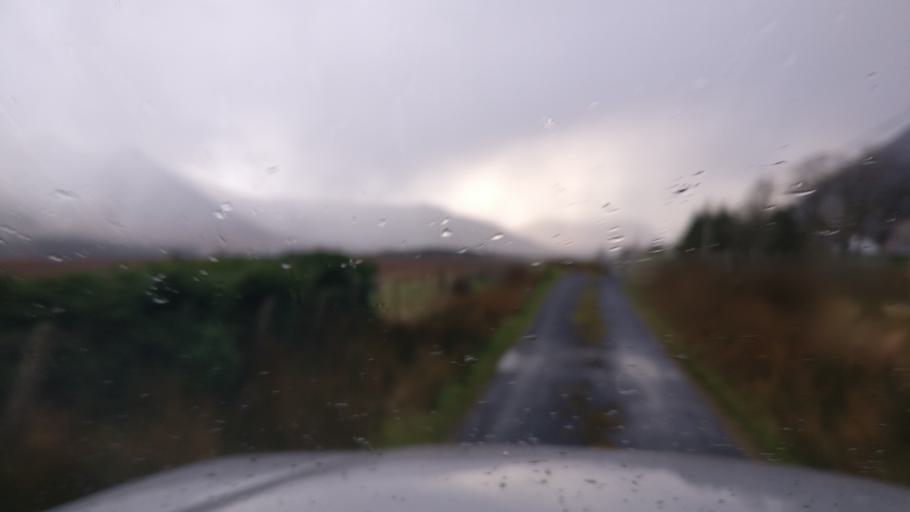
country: IE
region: Connaught
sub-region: County Galway
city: Clifden
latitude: 53.5132
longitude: -9.7120
